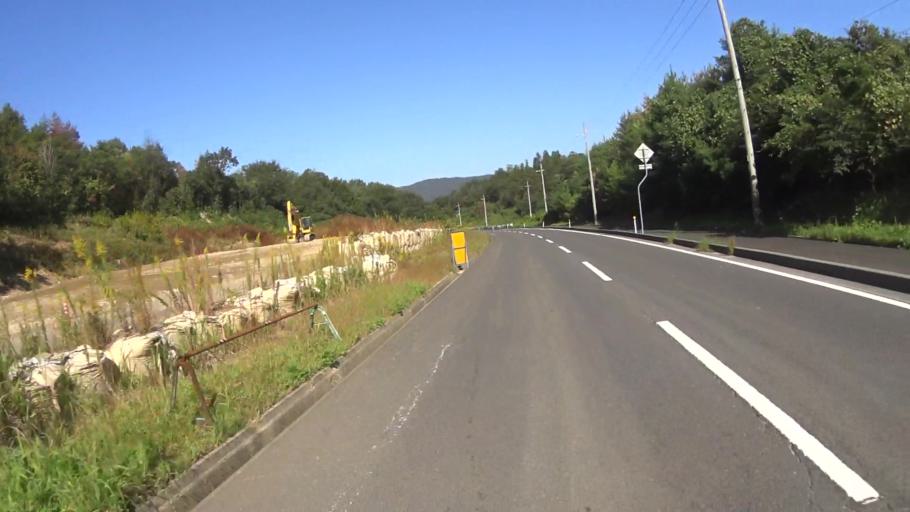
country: JP
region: Kyoto
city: Miyazu
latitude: 35.6647
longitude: 135.1025
